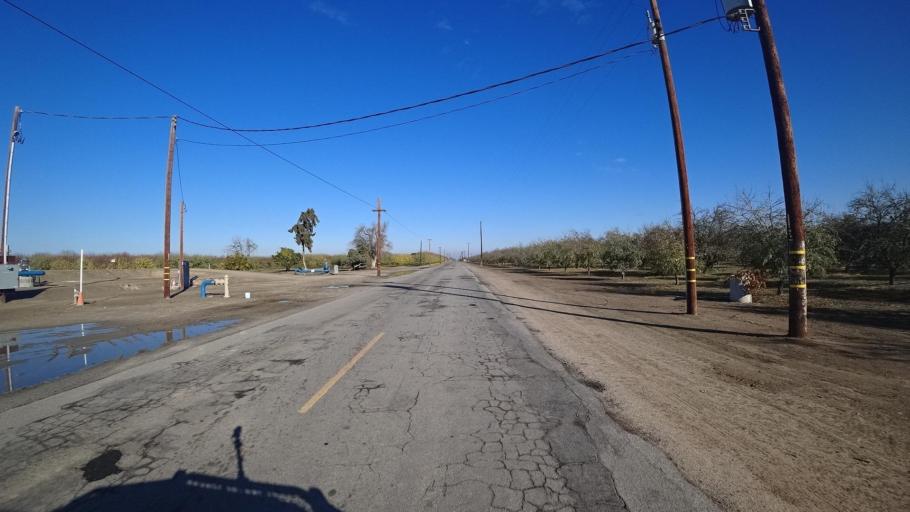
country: US
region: California
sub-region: Kern County
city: Delano
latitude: 35.7287
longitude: -119.3119
